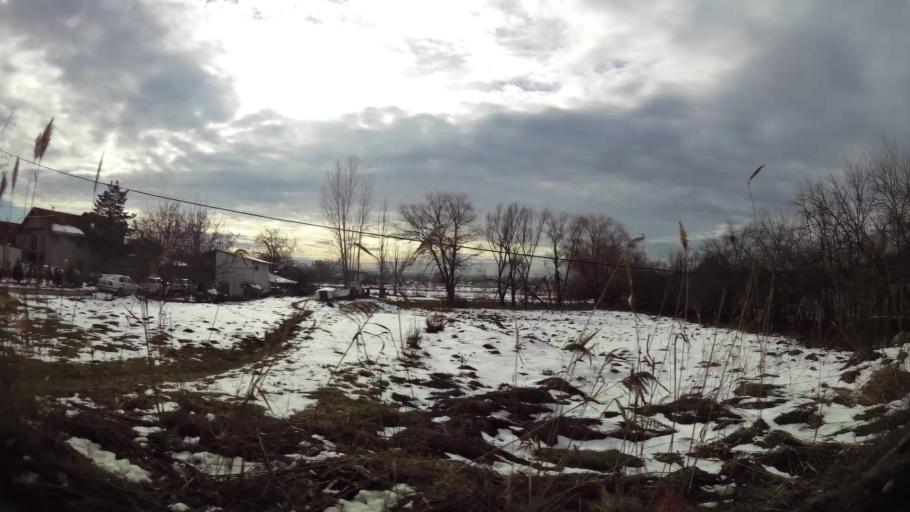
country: RS
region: Central Serbia
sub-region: Belgrade
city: Surcin
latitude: 44.7945
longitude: 20.3264
